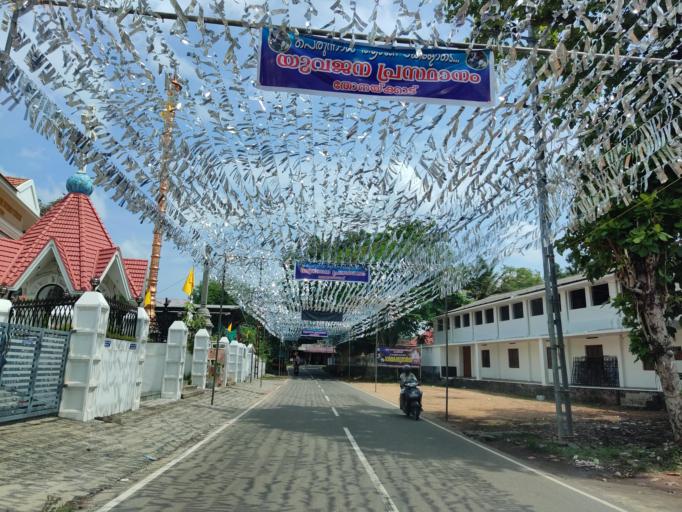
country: IN
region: Kerala
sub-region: Alappuzha
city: Mavelikara
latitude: 9.2771
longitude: 76.5672
